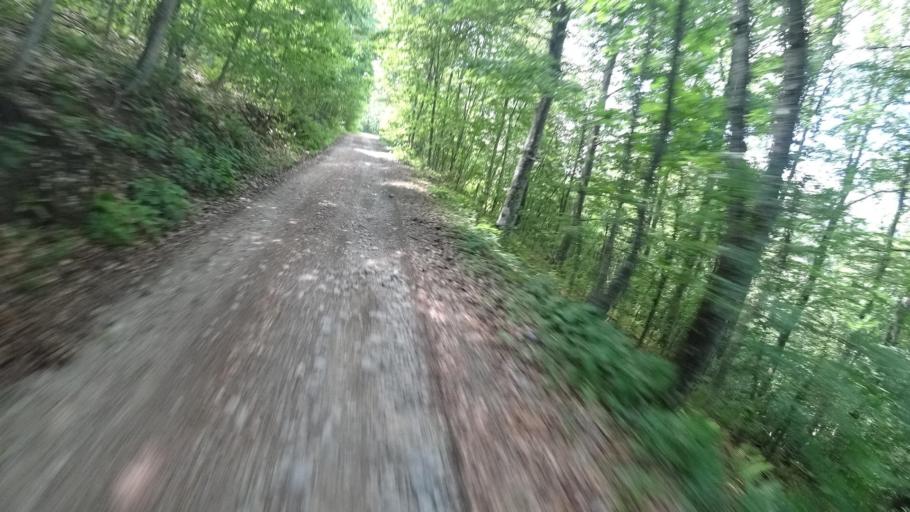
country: BA
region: Federation of Bosnia and Herzegovina
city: Ostrozac
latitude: 44.8330
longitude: 15.9963
